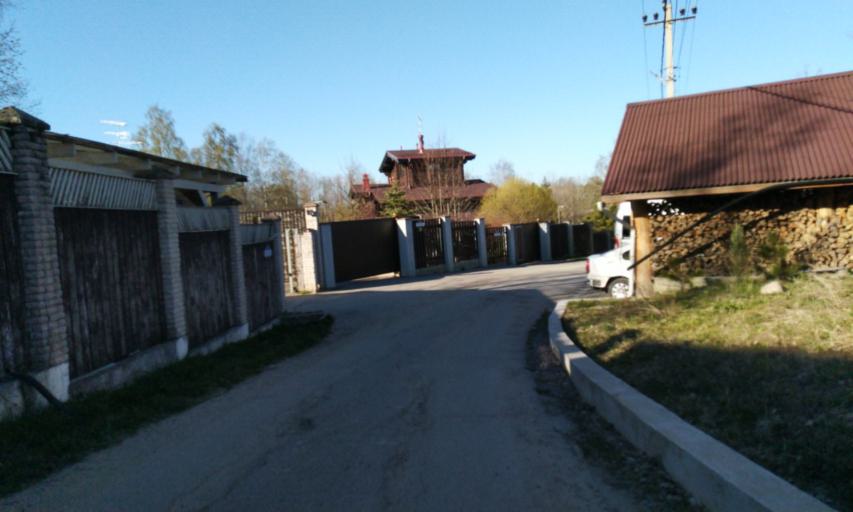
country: RU
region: Leningrad
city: Toksovo
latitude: 60.1516
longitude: 30.5706
